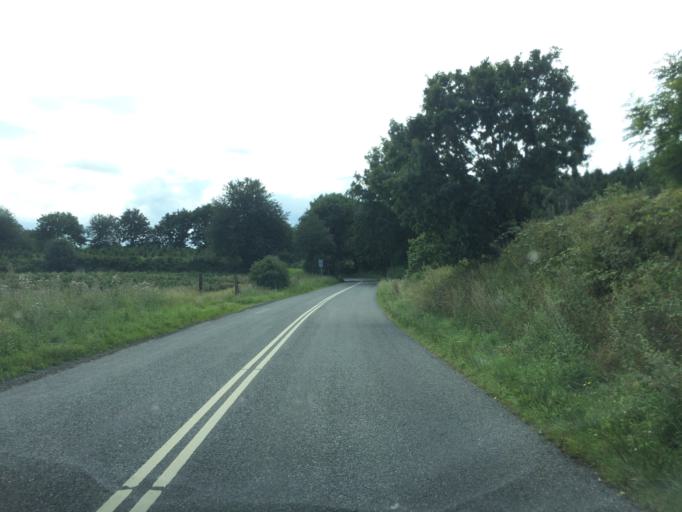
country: DK
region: South Denmark
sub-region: Faaborg-Midtfyn Kommune
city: Faaborg
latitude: 55.1541
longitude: 10.2636
